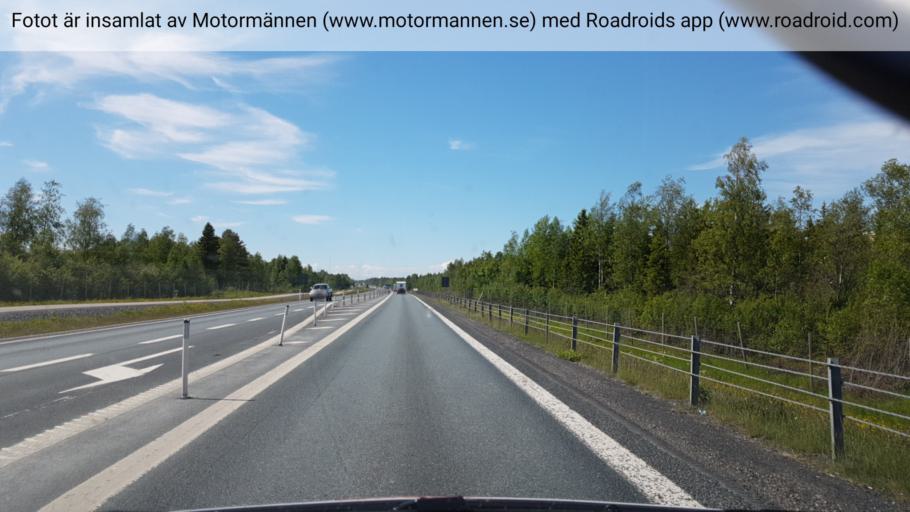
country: SE
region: Norrbotten
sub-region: Haparanda Kommun
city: Haparanda
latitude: 65.8110
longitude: 23.9421
